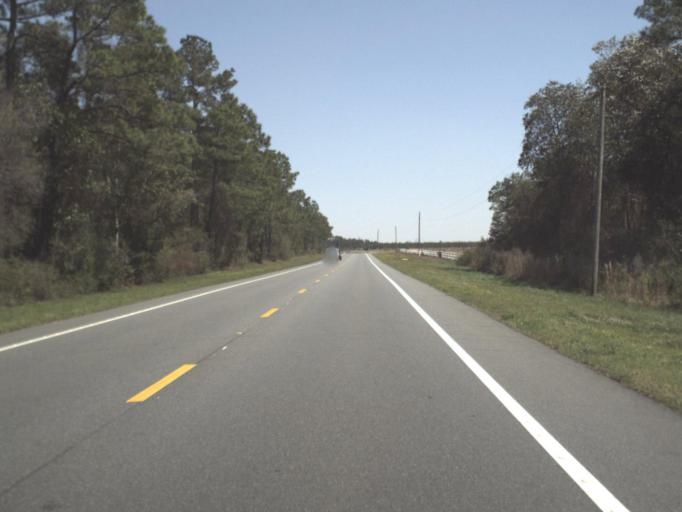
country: US
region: Florida
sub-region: Bay County
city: Youngstown
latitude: 30.4351
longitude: -85.3651
